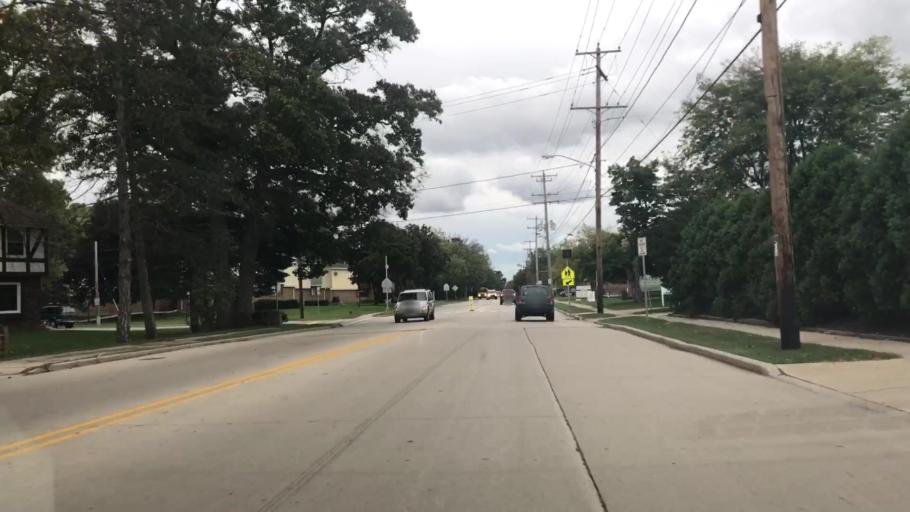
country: US
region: Wisconsin
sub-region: Waukesha County
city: Mukwonago
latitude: 42.8715
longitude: -88.3366
